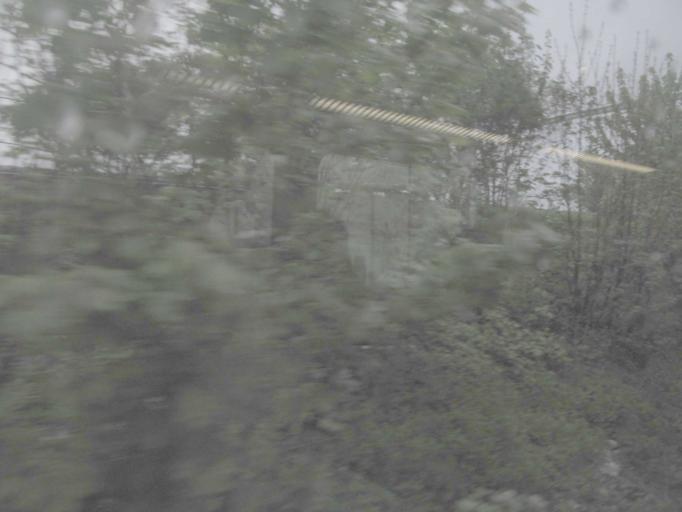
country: GB
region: England
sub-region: Reading
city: Reading
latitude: 51.4584
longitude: -0.9630
